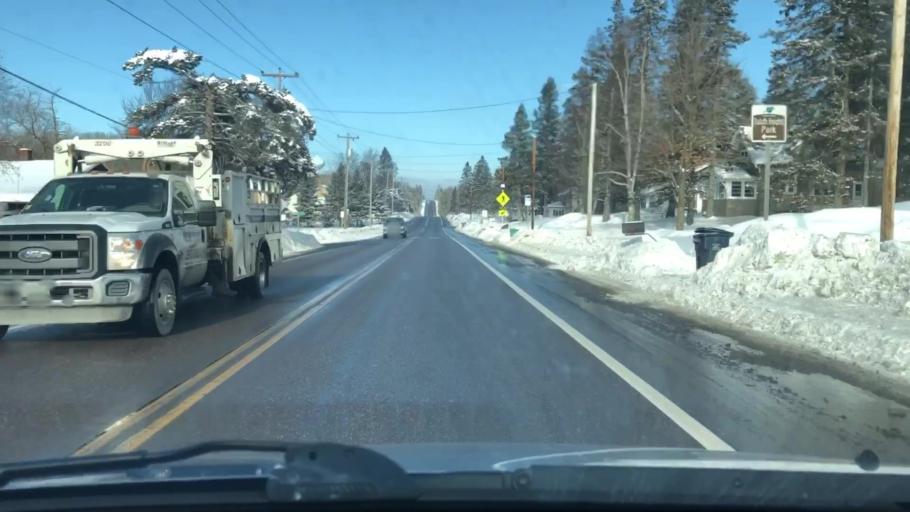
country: US
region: Minnesota
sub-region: Saint Louis County
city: Duluth
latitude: 46.8034
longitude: -92.1322
